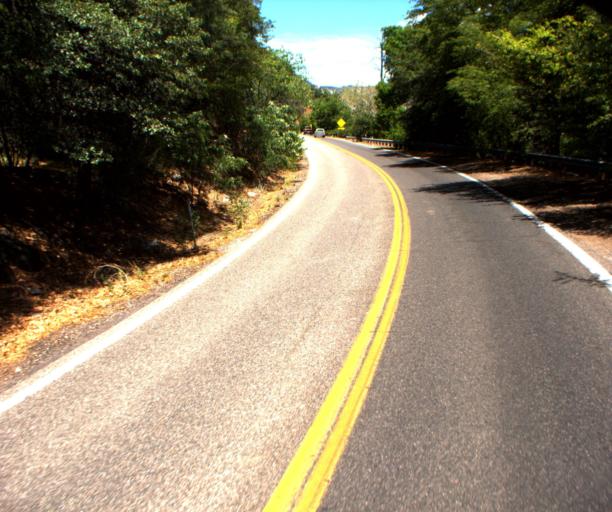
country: US
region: Arizona
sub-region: Coconino County
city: Sedona
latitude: 34.9137
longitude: -111.7282
